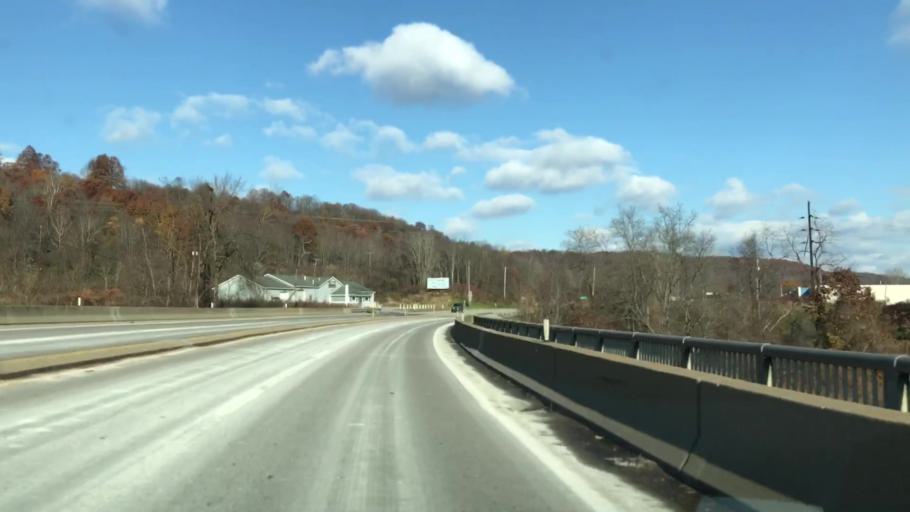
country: US
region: Pennsylvania
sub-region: Beaver County
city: West Mayfield
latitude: 40.7892
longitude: -80.3336
